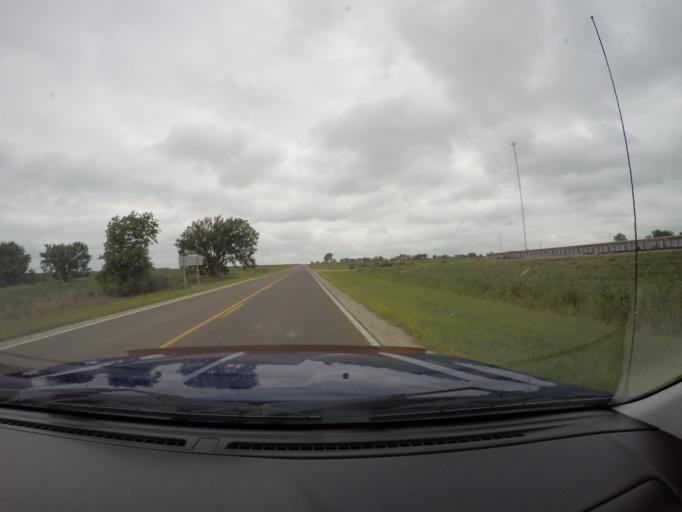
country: US
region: Kansas
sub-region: Morris County
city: Council Grove
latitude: 38.8551
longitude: -96.4912
